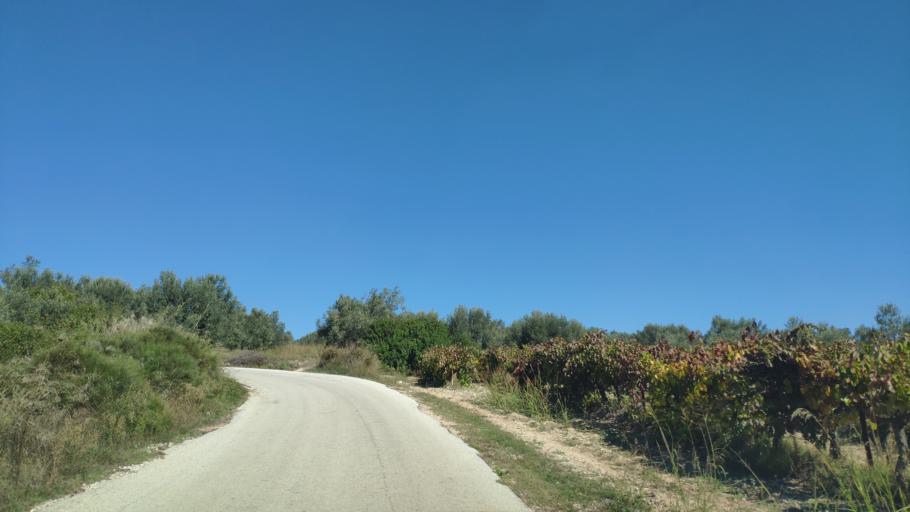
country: GR
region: Peloponnese
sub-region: Nomos Korinthias
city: Athikia
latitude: 37.8389
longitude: 22.9176
